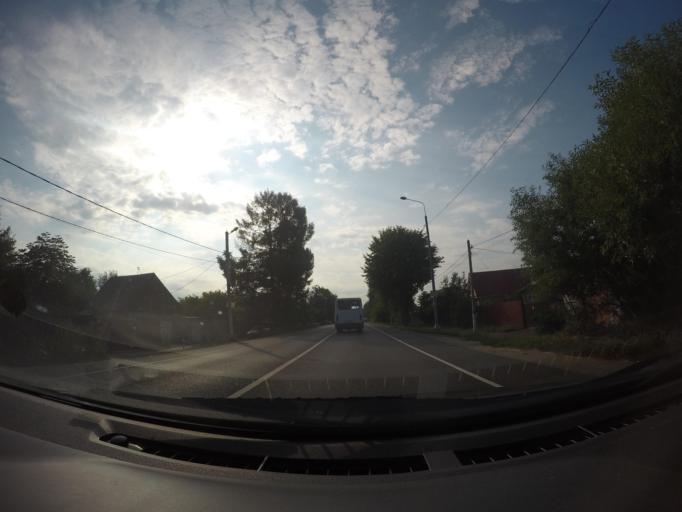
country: RU
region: Moskovskaya
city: Gzhel'
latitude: 55.6203
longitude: 38.3794
